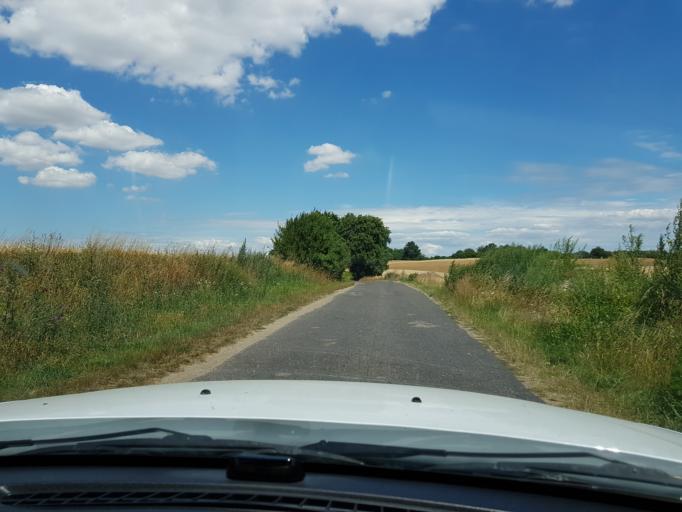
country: PL
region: West Pomeranian Voivodeship
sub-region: Powiat mysliborski
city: Barlinek
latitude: 52.9683
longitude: 15.1247
